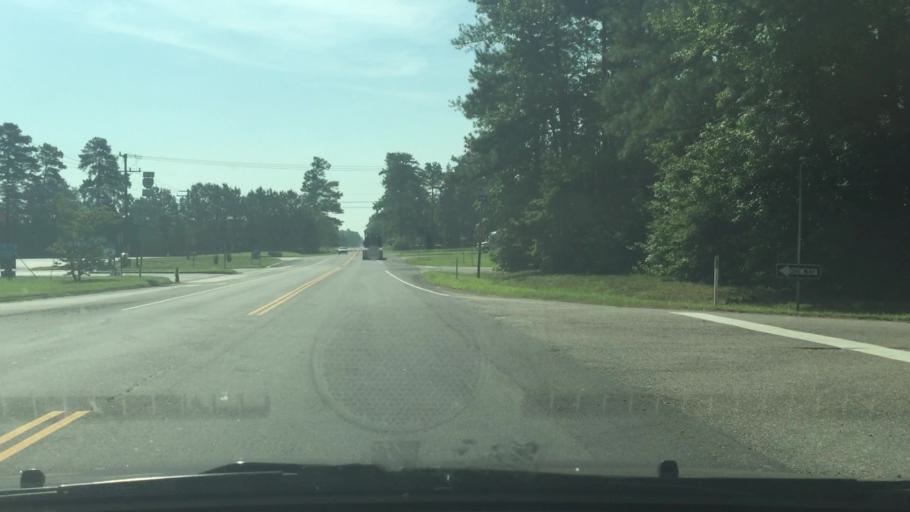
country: US
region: Virginia
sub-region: City of Petersburg
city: Petersburg
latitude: 37.0805
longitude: -77.3567
